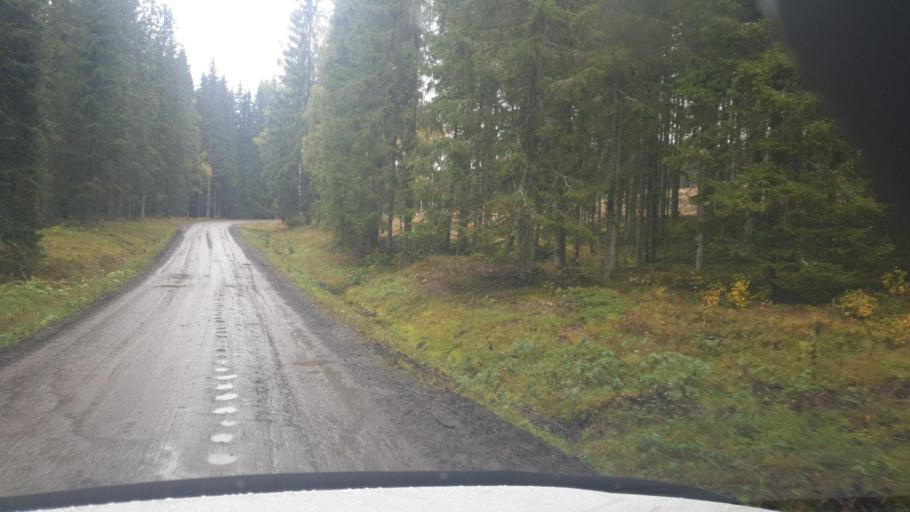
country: SE
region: Vaermland
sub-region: Sunne Kommun
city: Sunne
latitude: 59.8570
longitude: 12.8892
